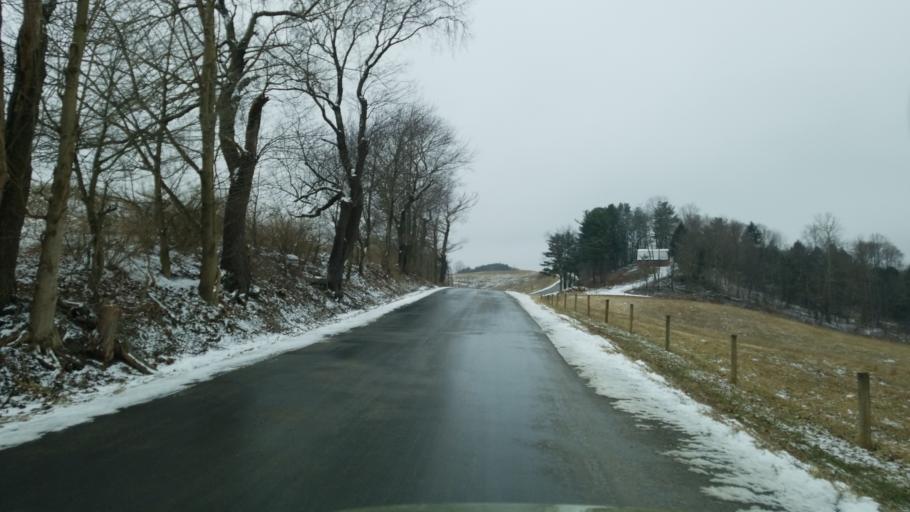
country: US
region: Pennsylvania
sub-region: Jefferson County
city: Sykesville
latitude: 41.0830
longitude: -78.8164
